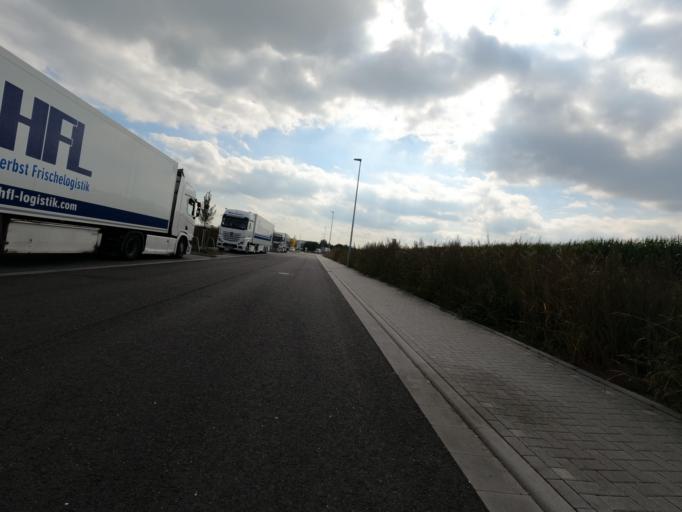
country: DE
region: North Rhine-Westphalia
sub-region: Regierungsbezirk Koln
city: Ubach-Palenberg
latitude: 50.9273
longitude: 6.1348
